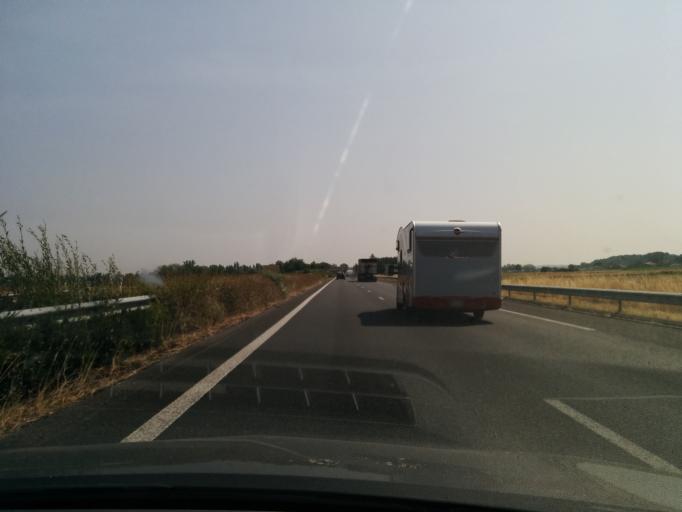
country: FR
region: Midi-Pyrenees
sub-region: Departement du Tarn
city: Brens
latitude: 43.8870
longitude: 1.9477
